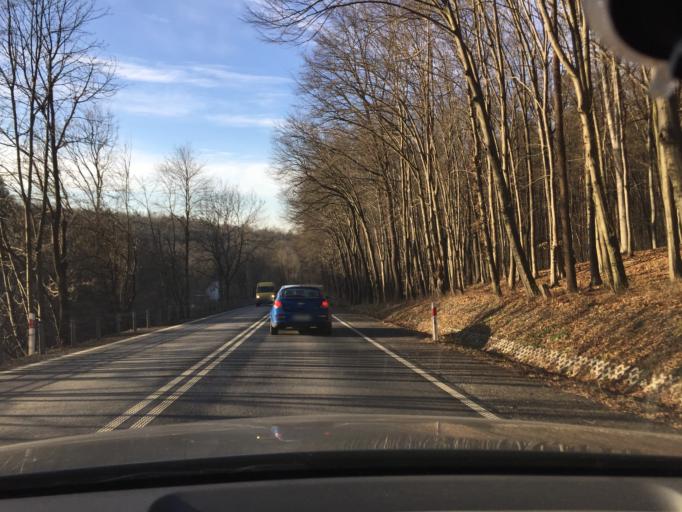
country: PL
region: Lesser Poland Voivodeship
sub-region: Powiat wadowicki
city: Lanckorona
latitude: 49.8654
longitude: 19.7279
